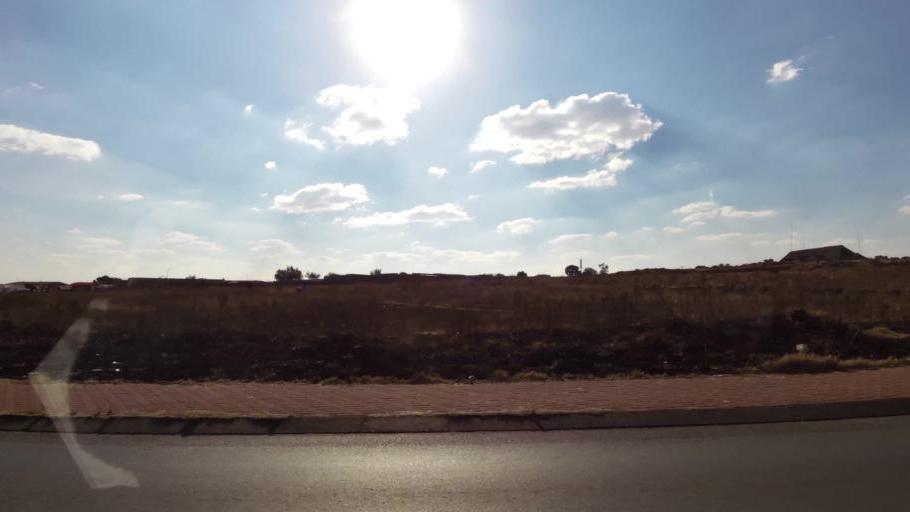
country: ZA
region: Gauteng
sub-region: City of Johannesburg Metropolitan Municipality
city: Soweto
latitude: -26.2244
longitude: 27.8864
